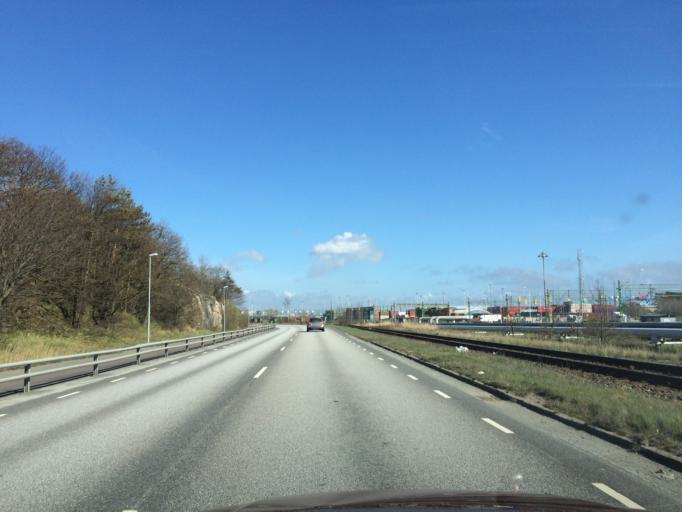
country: SE
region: Vaestra Goetaland
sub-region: Goteborg
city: Torslanda
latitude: 57.6969
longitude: 11.8384
